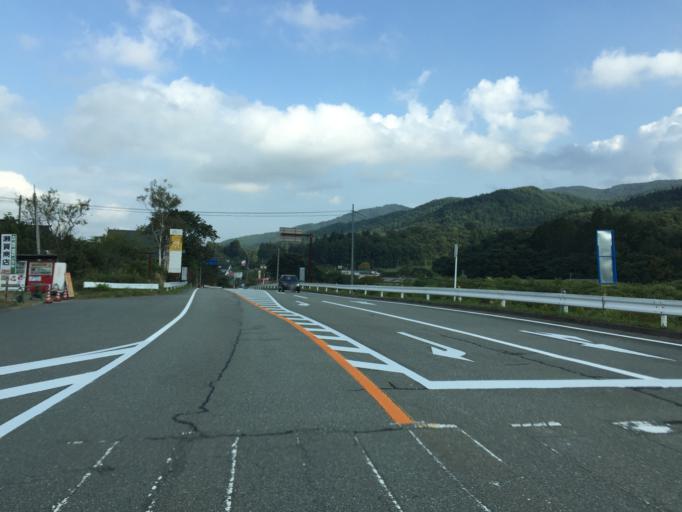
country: JP
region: Fukushima
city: Funehikimachi-funehiki
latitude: 37.5615
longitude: 140.7439
